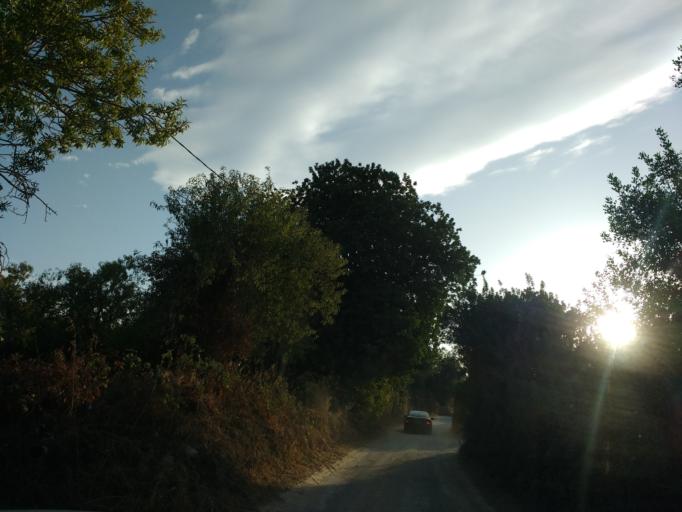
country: IT
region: Sicily
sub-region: Provincia di Siracusa
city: Noto
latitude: 36.8294
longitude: 15.0865
